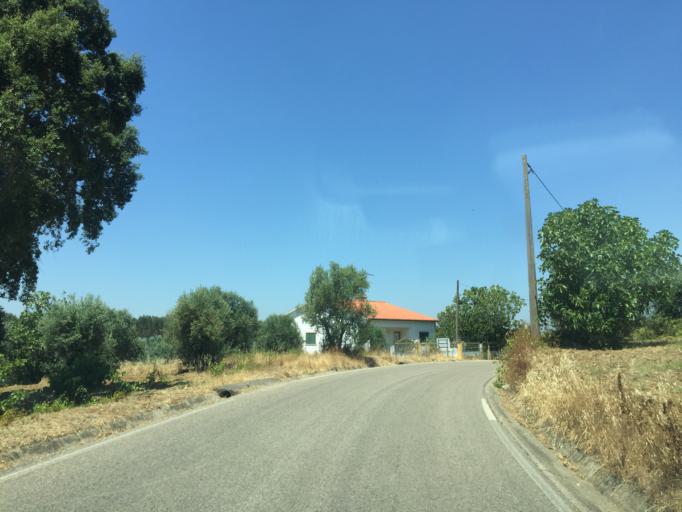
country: PT
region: Santarem
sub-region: Tomar
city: Tomar
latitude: 39.5944
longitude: -8.3298
